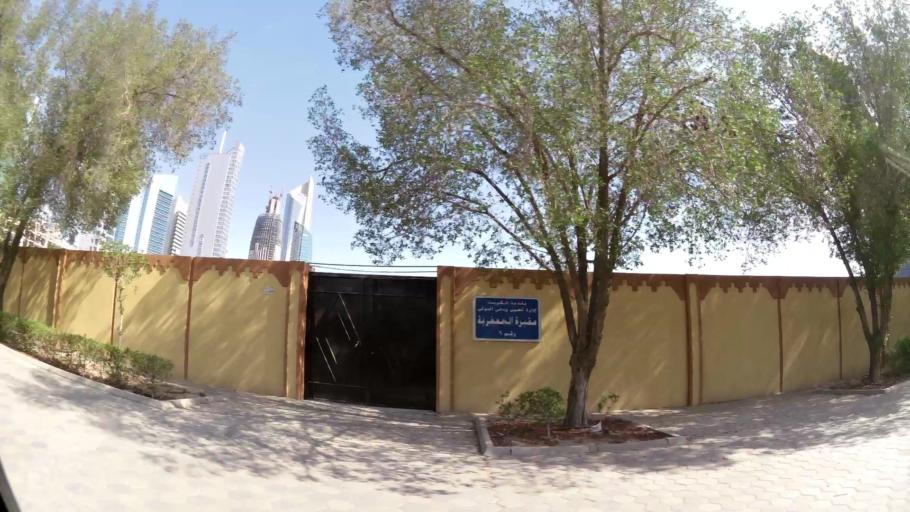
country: KW
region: Al Asimah
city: Kuwait City
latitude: 29.3710
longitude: 47.9890
